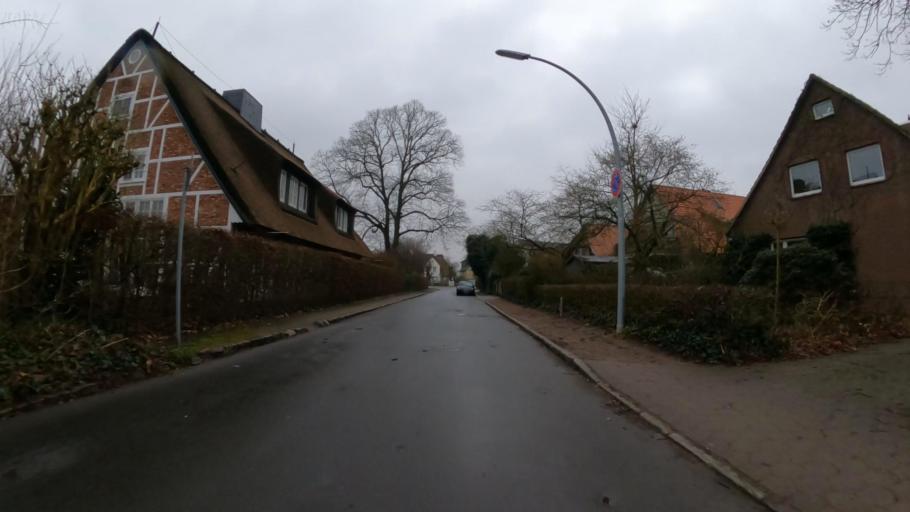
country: DE
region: Schleswig-Holstein
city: Rellingen
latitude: 53.5850
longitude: 9.7928
